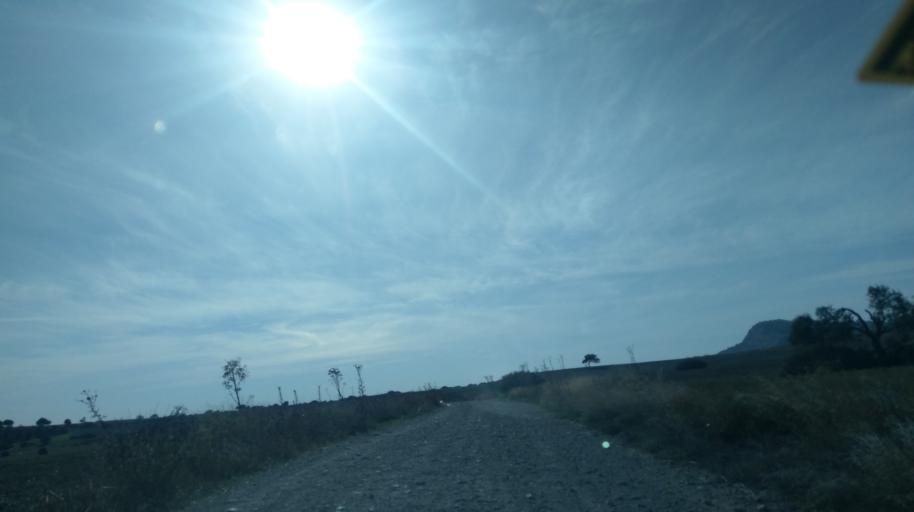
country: CY
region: Ammochostos
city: Trikomo
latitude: 35.3353
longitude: 33.8331
